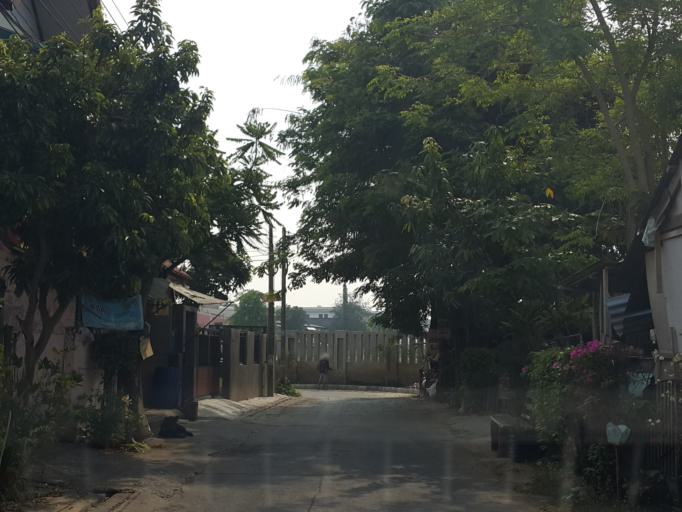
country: TH
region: Chiang Mai
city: Chiang Mai
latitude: 18.7594
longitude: 98.9849
